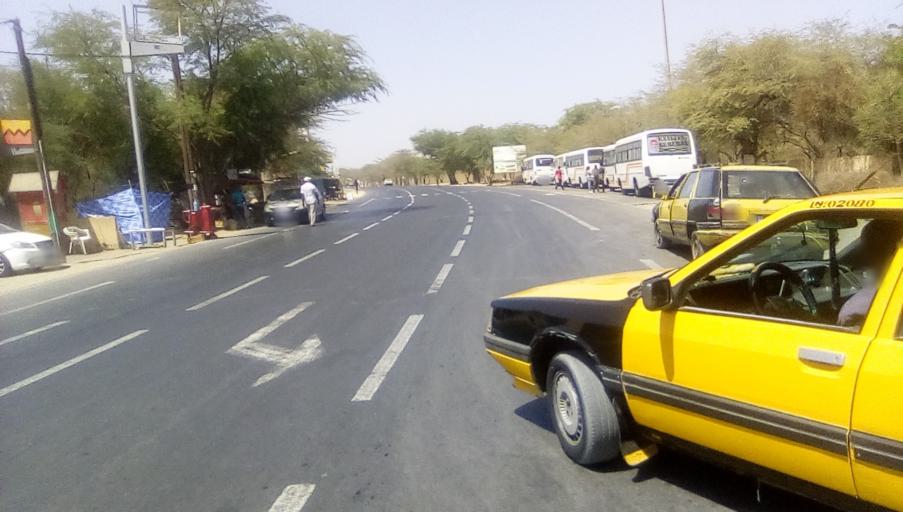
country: SN
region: Saint-Louis
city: Saint-Louis
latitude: 16.0602
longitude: -16.4217
